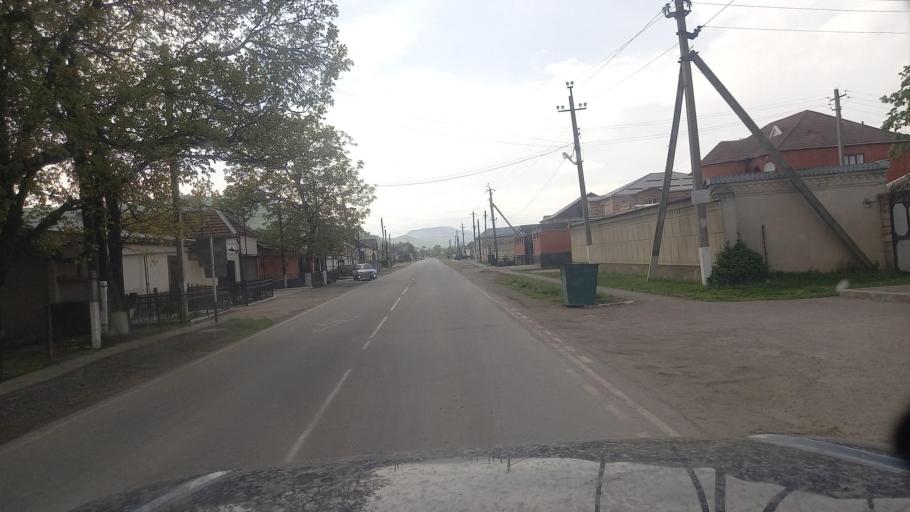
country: RU
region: Kabardino-Balkariya
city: Sarmakovo
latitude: 43.7301
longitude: 43.1624
